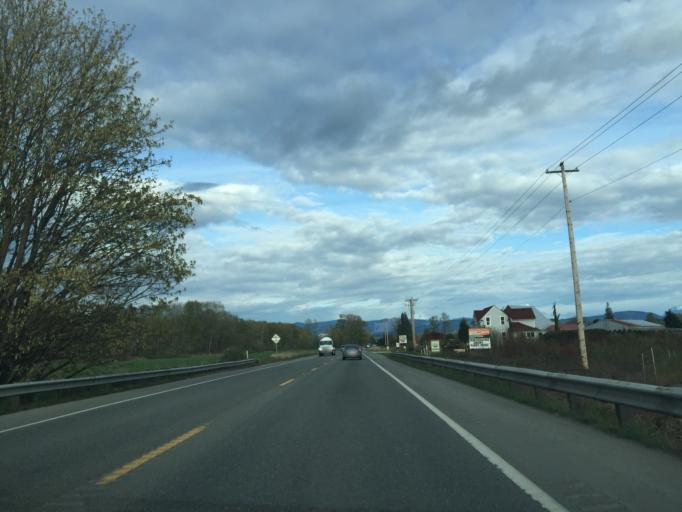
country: US
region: Washington
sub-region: Snohomish County
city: Smokey Point
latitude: 48.1884
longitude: -122.1861
